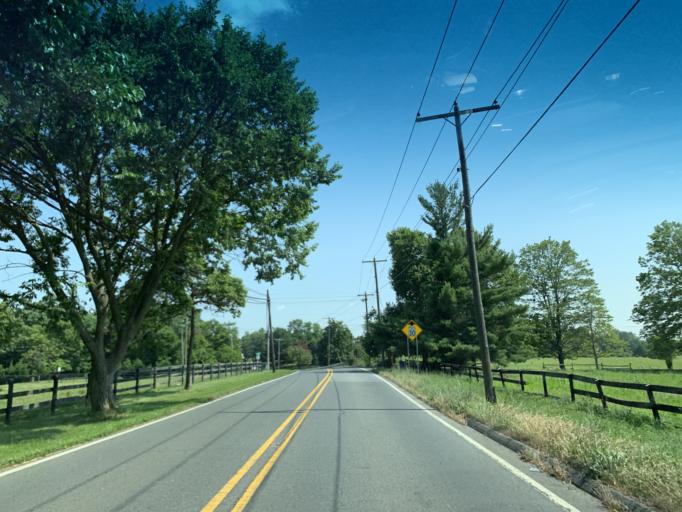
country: US
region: Maryland
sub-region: Montgomery County
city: Poolesville
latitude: 39.1550
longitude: -77.4181
